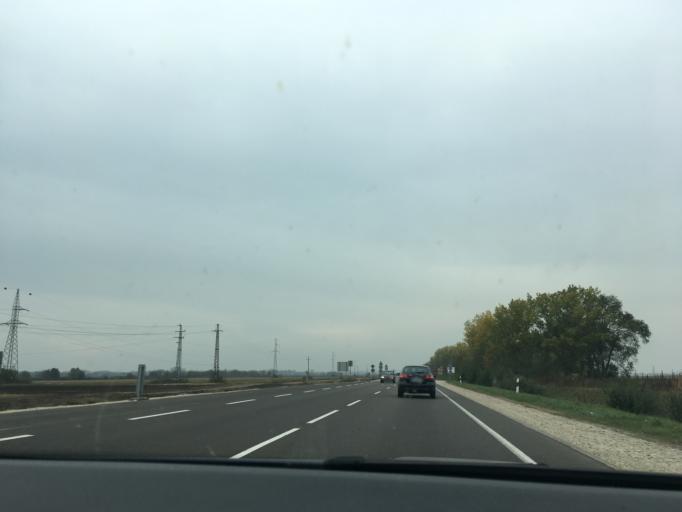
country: HU
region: Pest
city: Cegled
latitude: 47.2054
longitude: 19.7704
